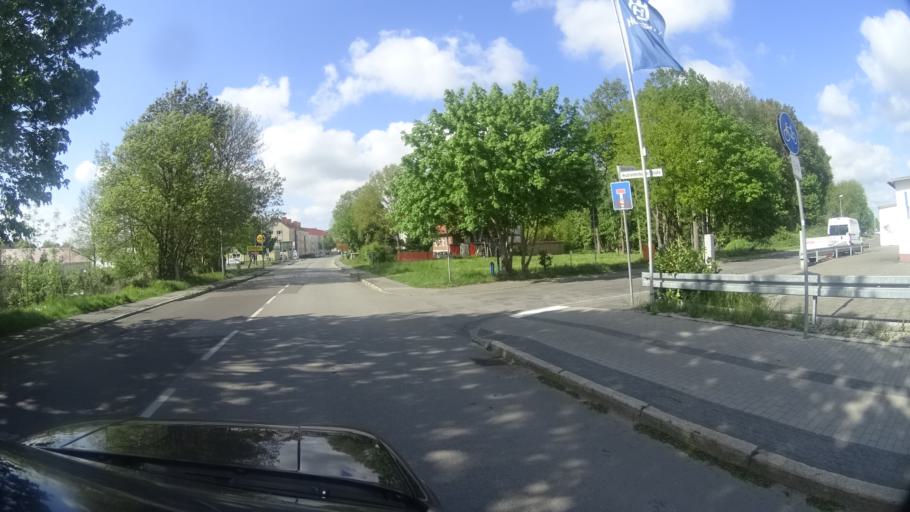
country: DE
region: Mecklenburg-Vorpommern
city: Rostock
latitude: 54.0787
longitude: 12.1604
